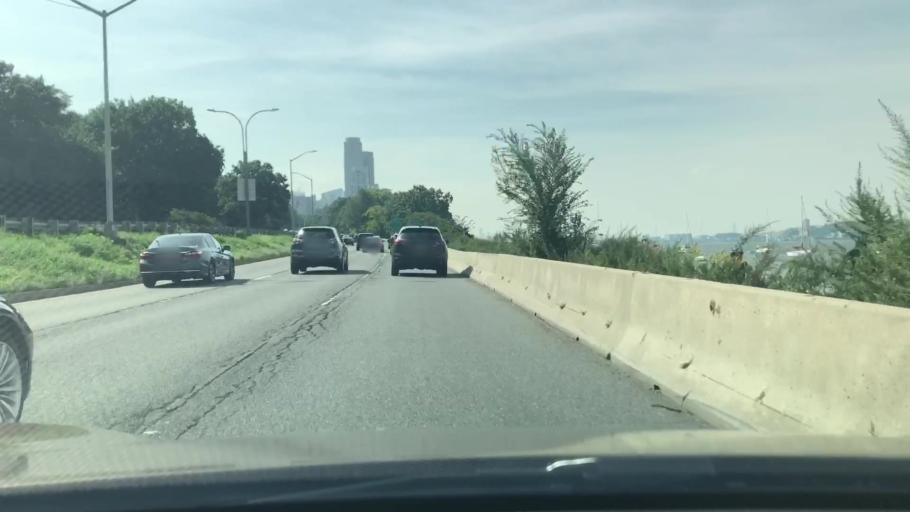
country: US
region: New York
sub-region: New York County
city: Manhattan
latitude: 40.7908
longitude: -73.9816
